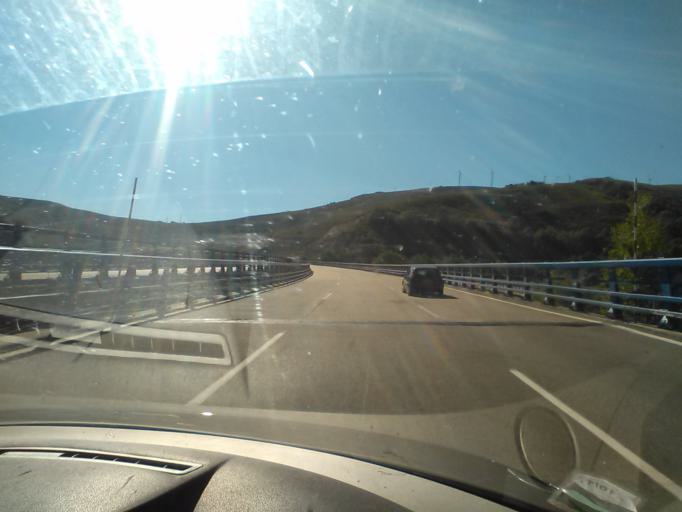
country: ES
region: Castille and Leon
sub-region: Provincia de Zamora
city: Lubian
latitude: 42.0392
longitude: -6.9504
